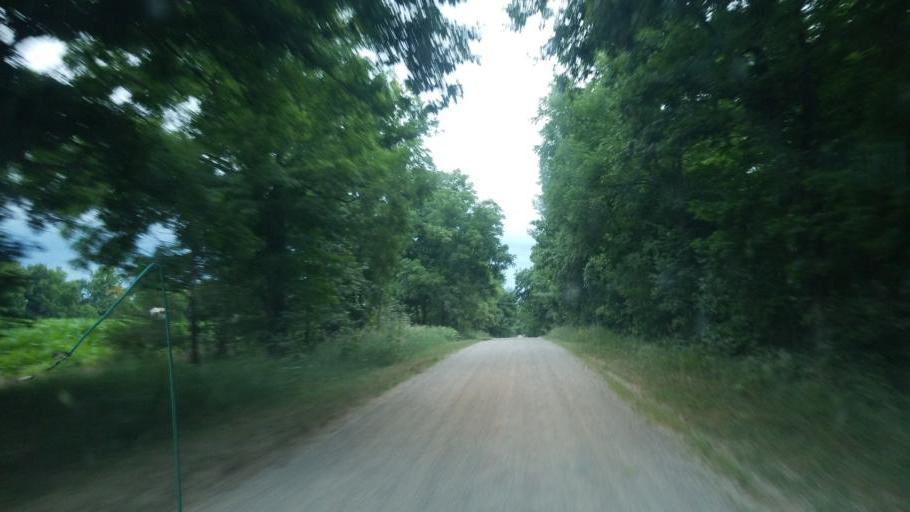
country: US
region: Ohio
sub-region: Defiance County
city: Hicksville
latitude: 41.3288
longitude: -84.8224
